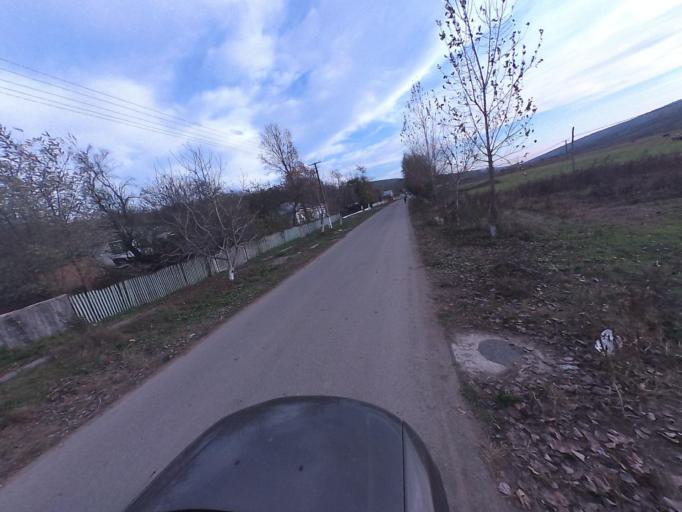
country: RO
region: Vaslui
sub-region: Comuna Gherghesti
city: Gherghesti
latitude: 46.4900
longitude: 27.5338
